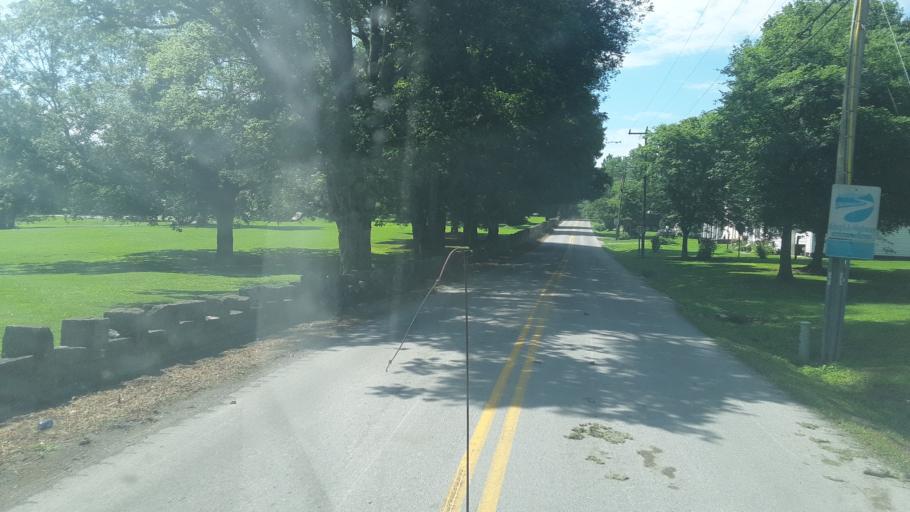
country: US
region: Kentucky
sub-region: Todd County
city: Elkton
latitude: 36.8433
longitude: -87.3010
